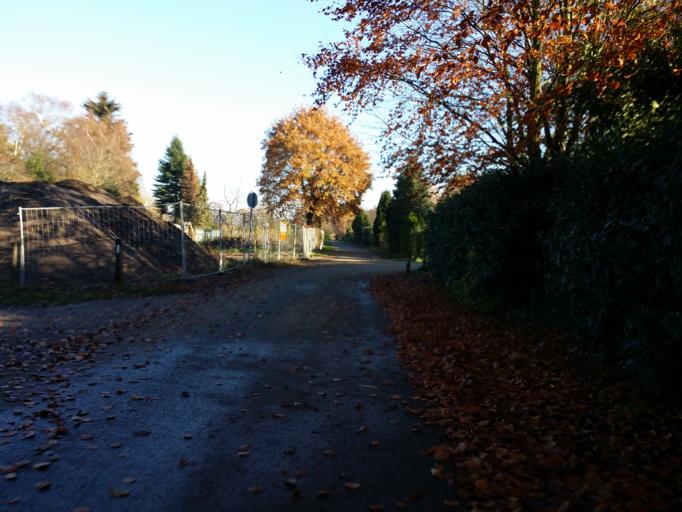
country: DE
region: Lower Saxony
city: Lilienthal
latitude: 53.0797
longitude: 8.9418
